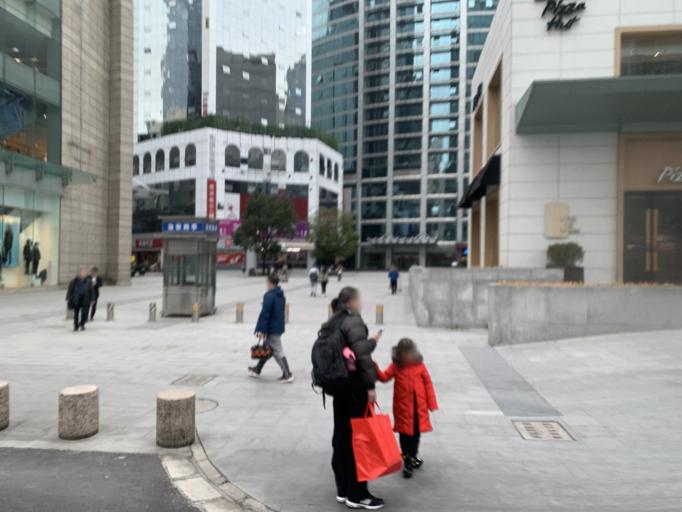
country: CN
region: Shanghai Shi
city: Pudong
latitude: 31.2308
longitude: 121.5118
